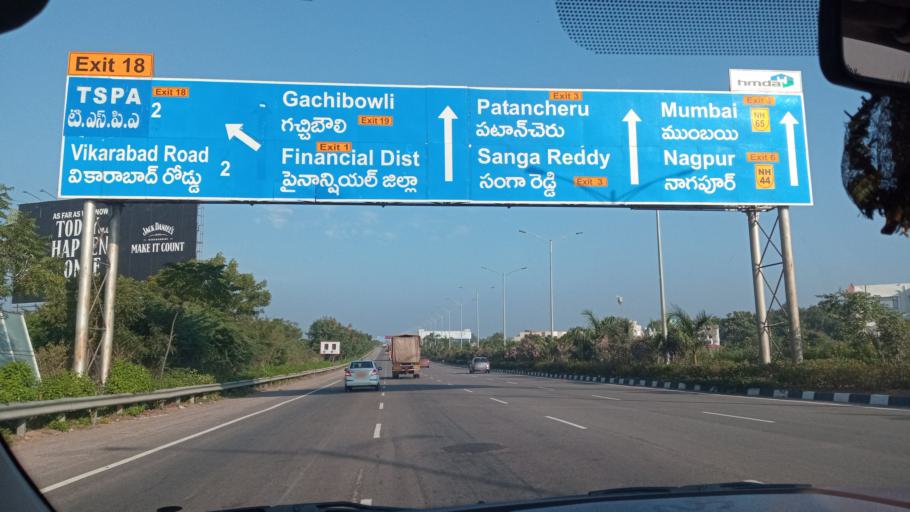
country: IN
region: Telangana
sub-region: Hyderabad
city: Hyderabad
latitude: 17.3309
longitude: 78.3710
